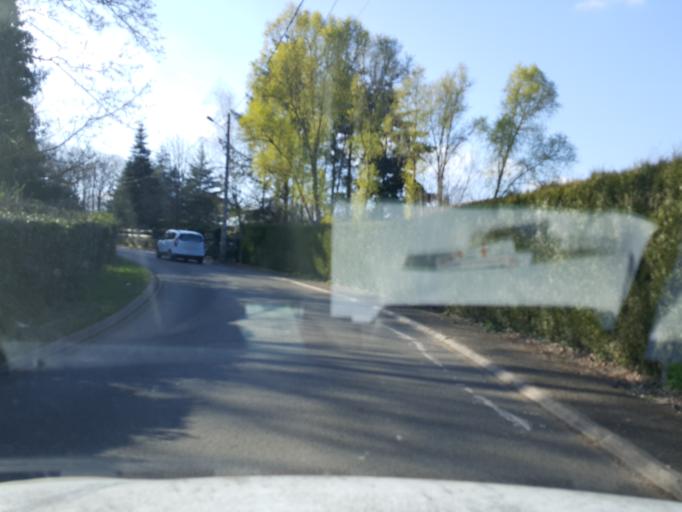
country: FR
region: Ile-de-France
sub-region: Departement des Yvelines
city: Gazeran
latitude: 48.6352
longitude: 1.7655
